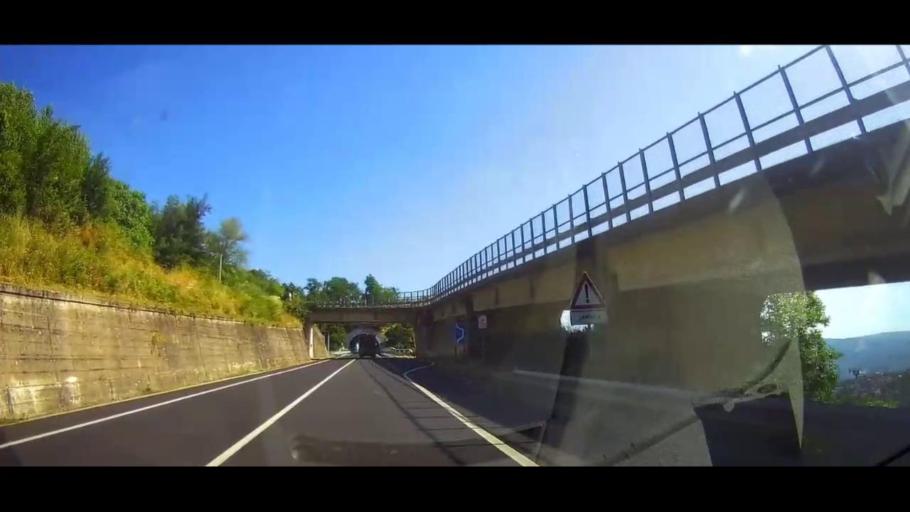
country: IT
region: Calabria
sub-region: Provincia di Cosenza
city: Spezzano della Sila
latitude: 39.2976
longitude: 16.3430
